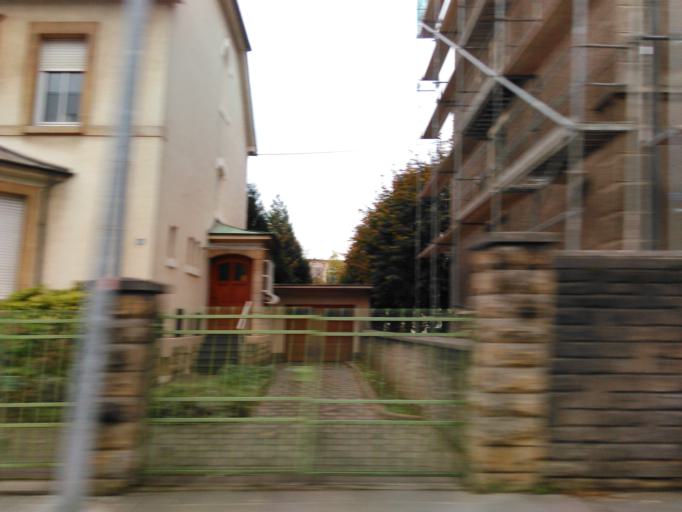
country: LU
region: Luxembourg
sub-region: Canton de Luxembourg
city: Luxembourg
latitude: 49.6189
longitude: 6.1175
